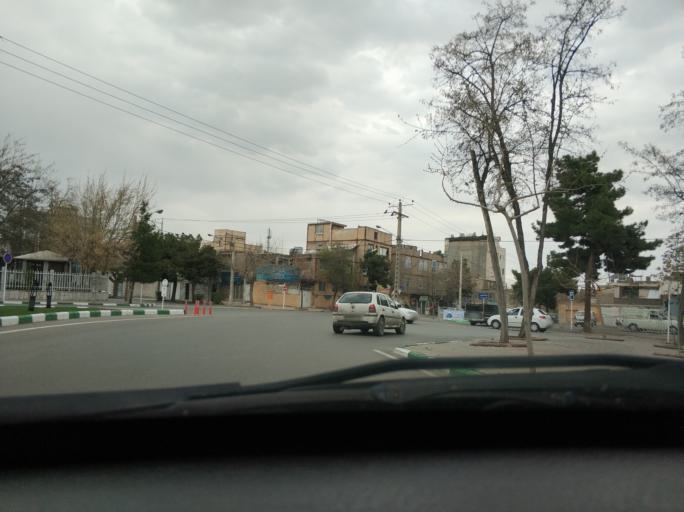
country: IR
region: Razavi Khorasan
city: Mashhad
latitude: 36.2570
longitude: 59.6106
